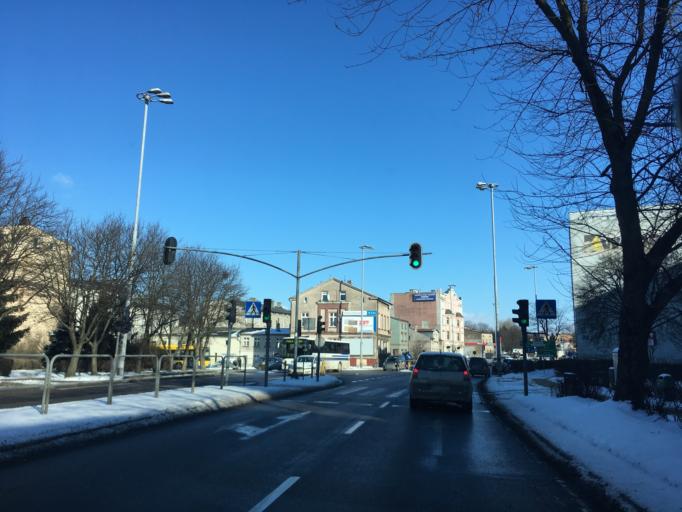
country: PL
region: Pomeranian Voivodeship
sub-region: Slupsk
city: Slupsk
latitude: 54.4649
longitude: 17.0376
